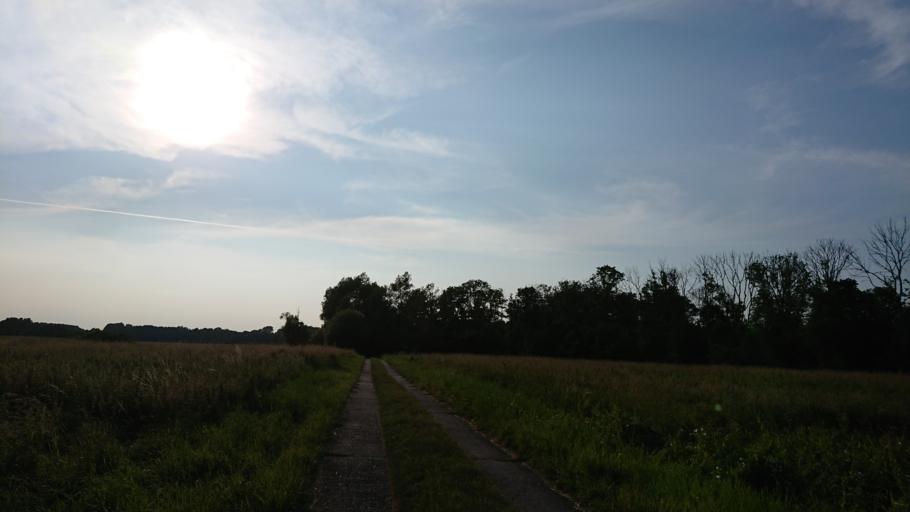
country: DE
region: Mecklenburg-Vorpommern
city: Gormin
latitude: 53.9740
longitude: 13.2924
